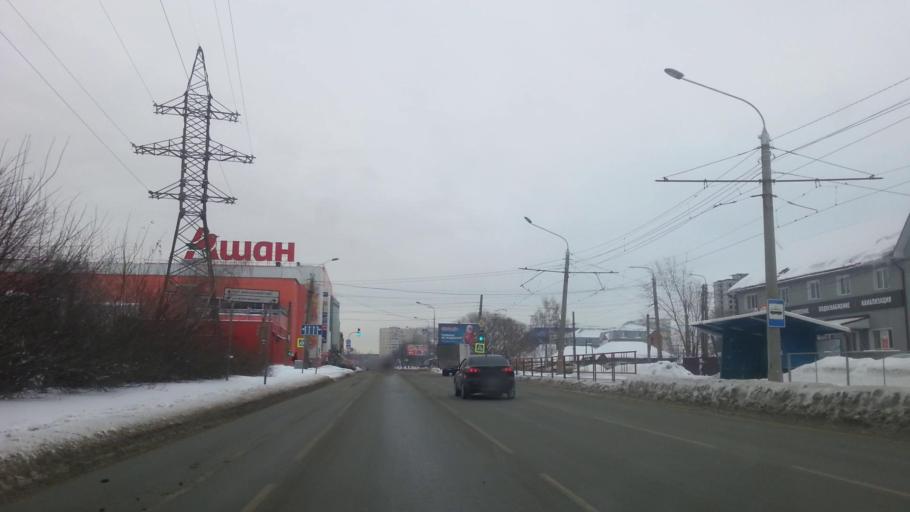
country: RU
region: Altai Krai
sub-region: Gorod Barnaulskiy
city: Barnaul
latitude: 53.3399
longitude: 83.7477
